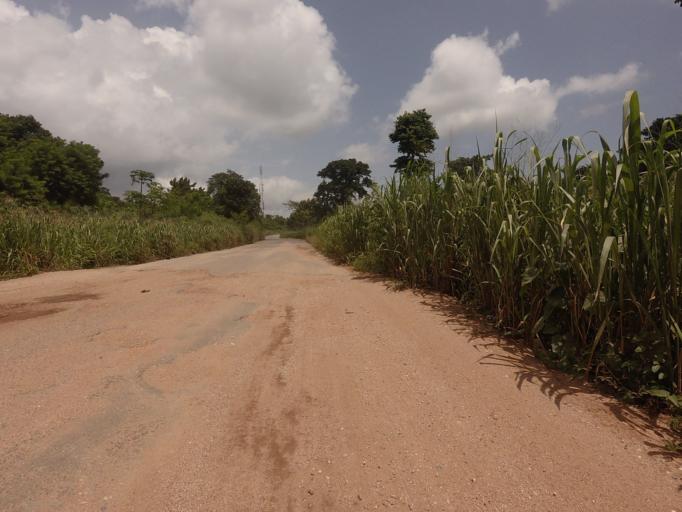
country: GH
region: Volta
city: Ho
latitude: 6.7192
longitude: 0.3400
